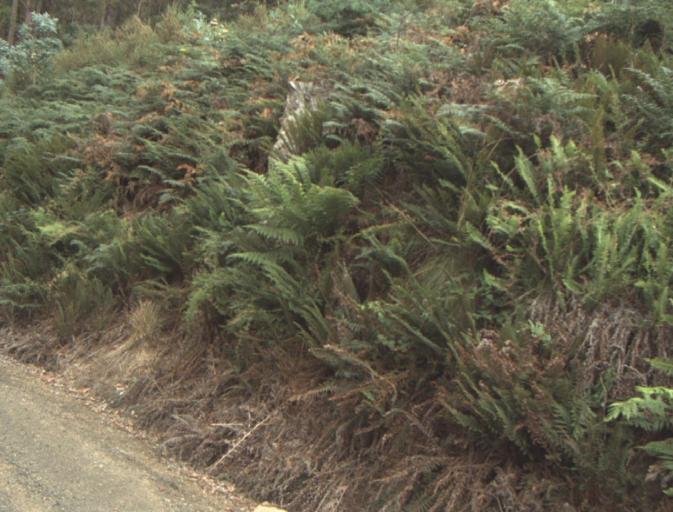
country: AU
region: Tasmania
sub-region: Northern Midlands
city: Evandale
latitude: -41.4557
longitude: 147.4720
